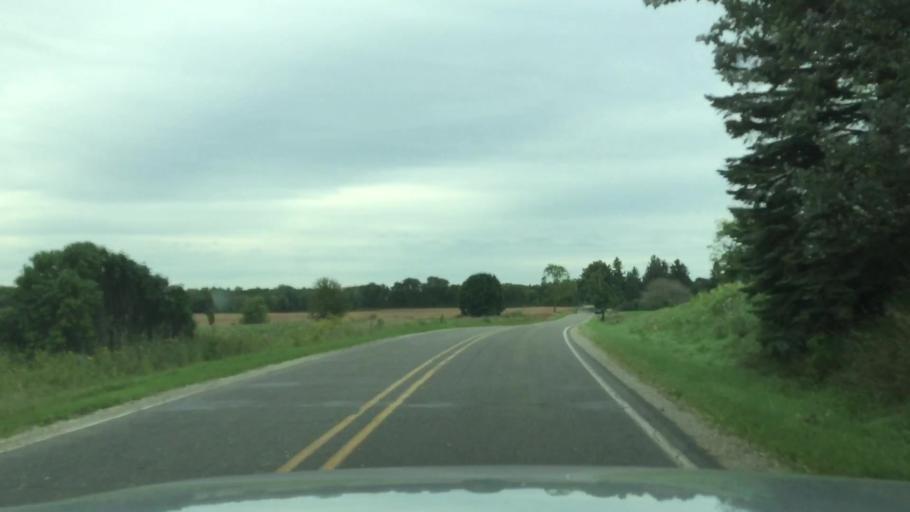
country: US
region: Michigan
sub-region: Shiawassee County
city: Durand
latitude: 42.8560
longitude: -84.0393
